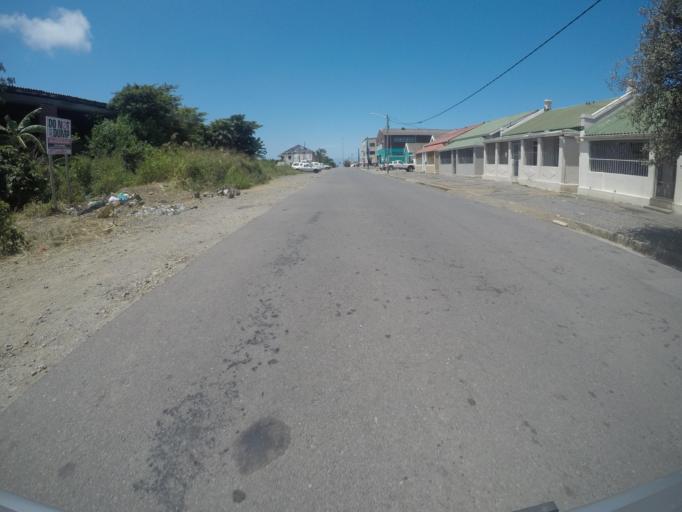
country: ZA
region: Eastern Cape
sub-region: Buffalo City Metropolitan Municipality
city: East London
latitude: -33.0135
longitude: 27.9107
